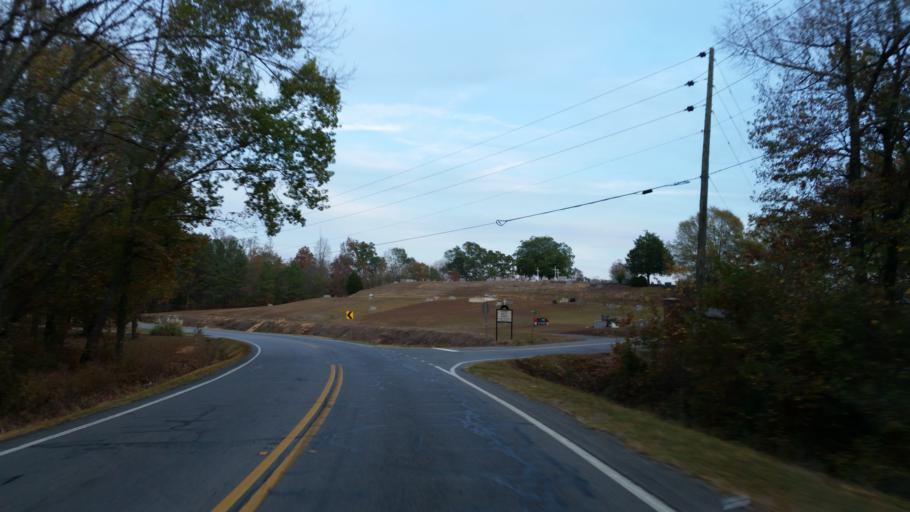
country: US
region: Georgia
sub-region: Gordon County
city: Calhoun
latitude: 34.5932
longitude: -84.8963
